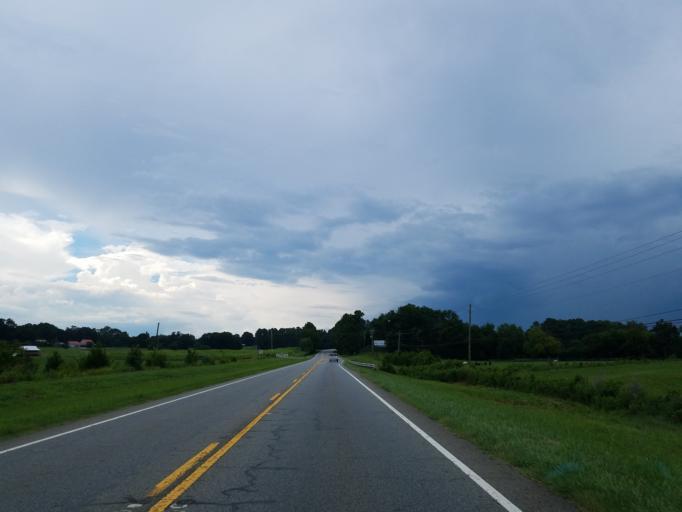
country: US
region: Georgia
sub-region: Bartow County
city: Adairsville
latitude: 34.2712
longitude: -84.8647
